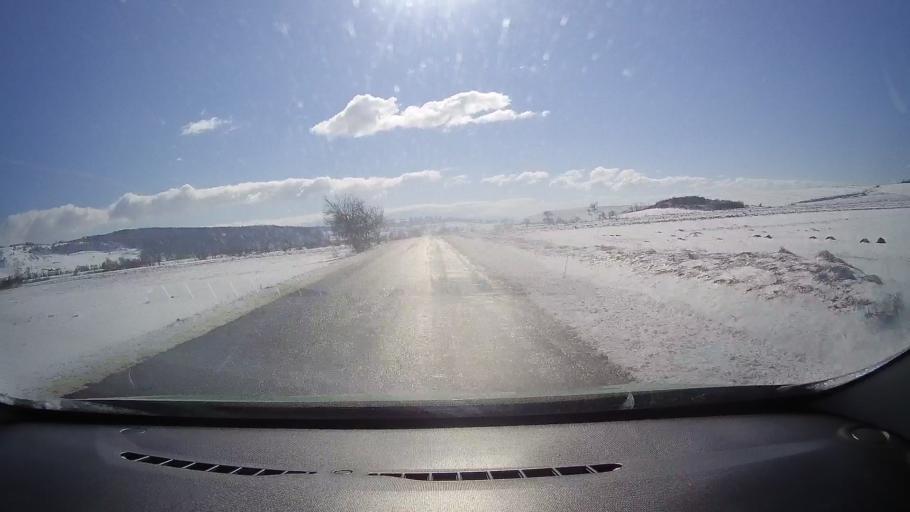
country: RO
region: Sibiu
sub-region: Comuna Vurpar
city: Vurpar
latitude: 45.8700
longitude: 24.3183
